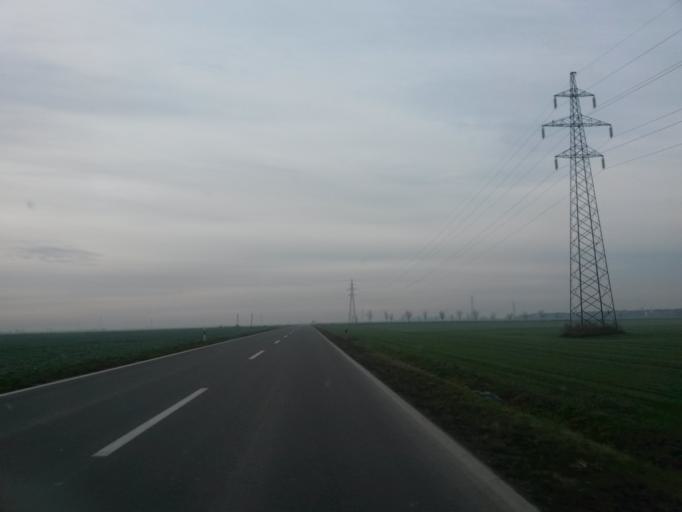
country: HR
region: Osjecko-Baranjska
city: Brijest
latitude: 45.5278
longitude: 18.6873
